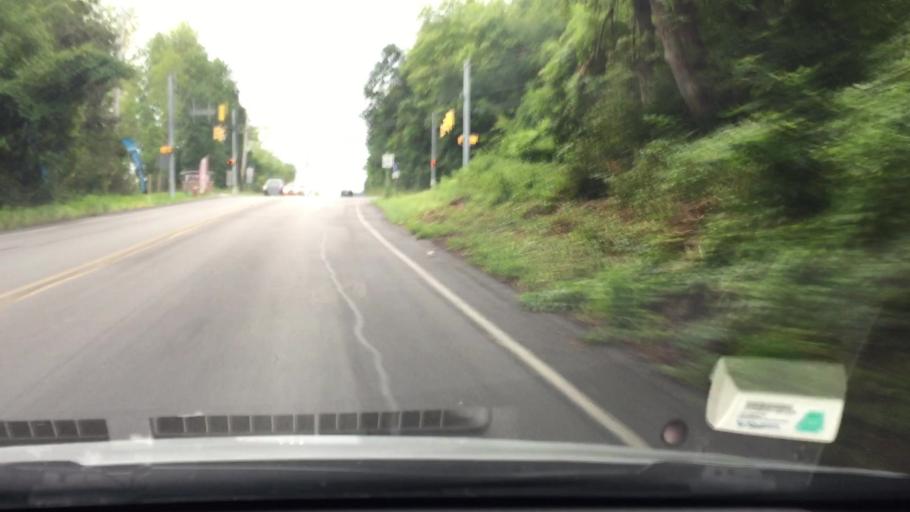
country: US
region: Pennsylvania
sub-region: Butler County
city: Cranberry Township
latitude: 40.6621
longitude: -80.0997
